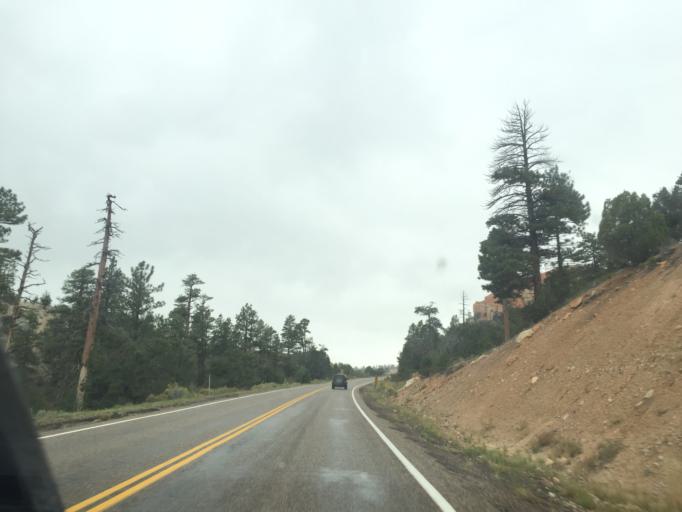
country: US
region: Utah
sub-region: Garfield County
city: Panguitch
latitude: 37.6844
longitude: -112.1194
